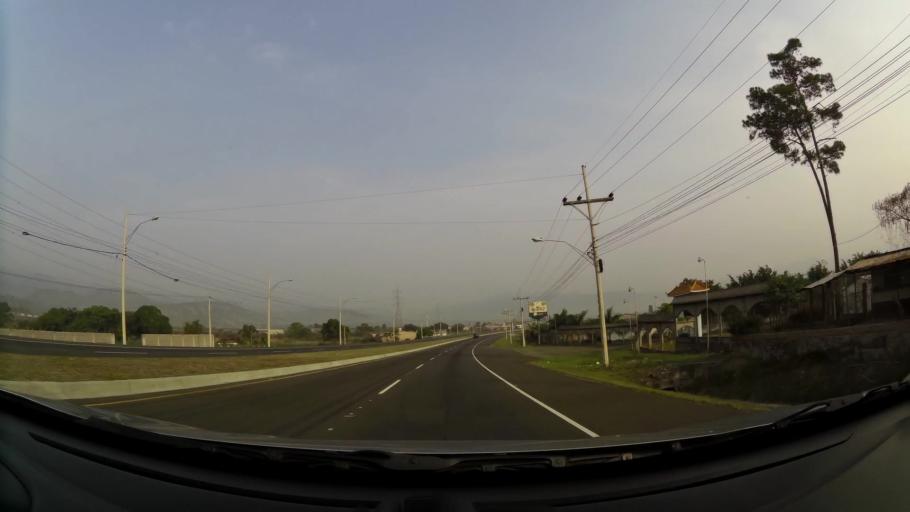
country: HN
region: Francisco Morazan
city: Tamara
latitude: 14.1990
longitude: -87.3432
